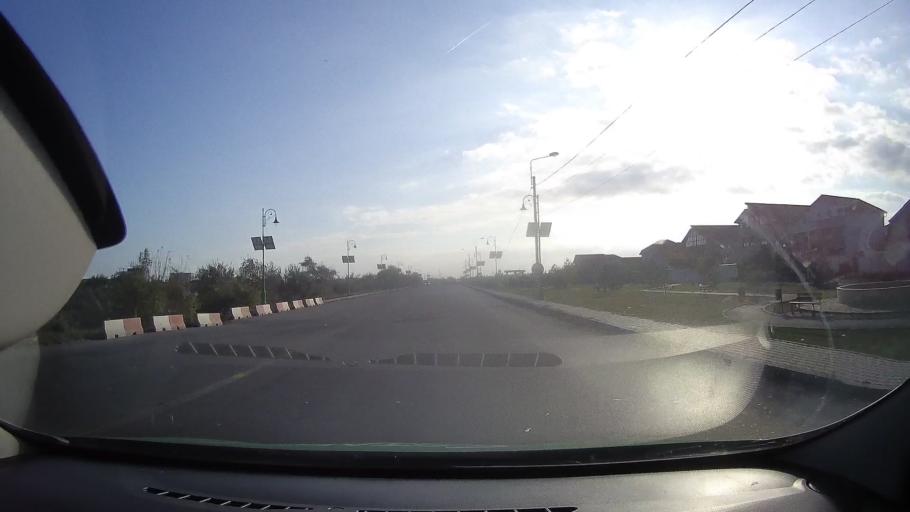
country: RO
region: Constanta
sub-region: Comuna Navodari
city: Navodari
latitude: 44.3106
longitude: 28.6160
